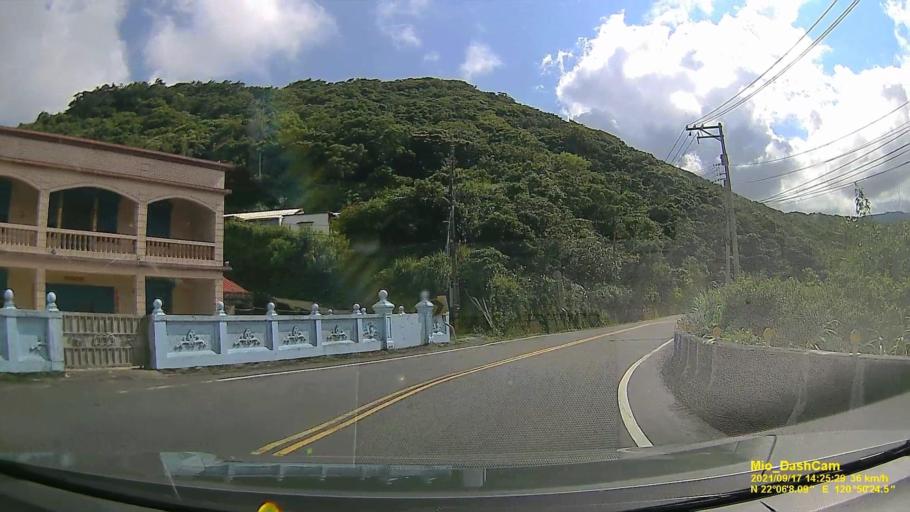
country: TW
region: Taiwan
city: Hengchun
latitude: 22.1023
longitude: 120.8401
